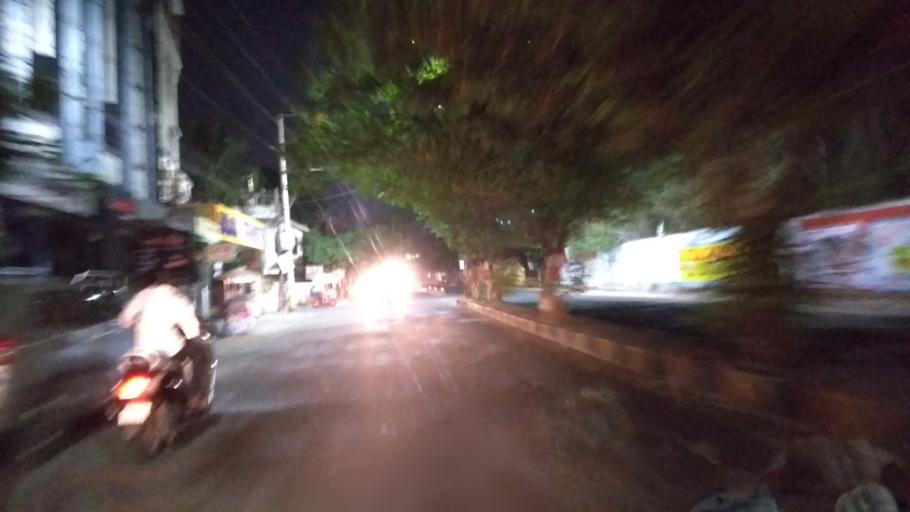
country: IN
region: Telangana
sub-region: Rangareddi
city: Kukatpalli
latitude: 17.4434
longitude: 78.4364
